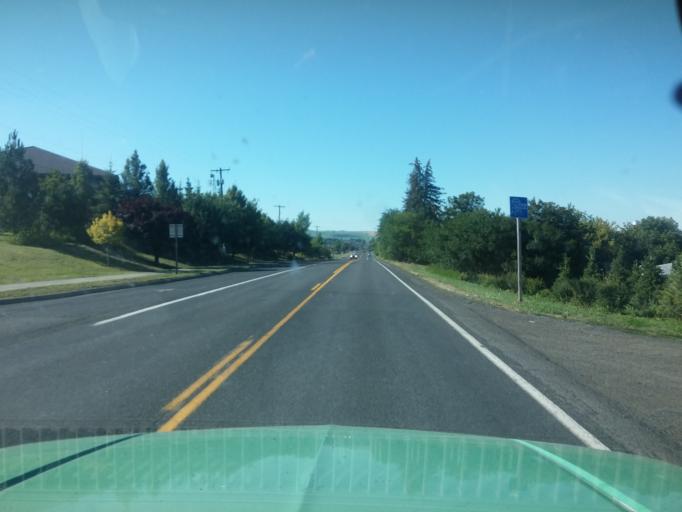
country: US
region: Idaho
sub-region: Latah County
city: Moscow
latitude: 46.7476
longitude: -117.0016
